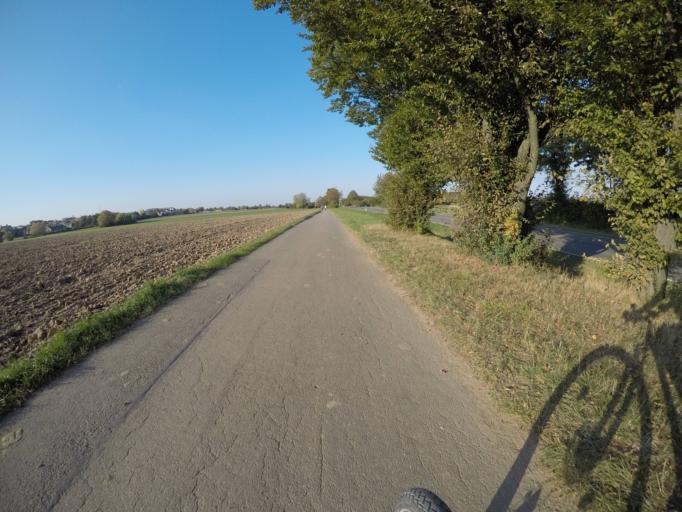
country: DE
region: Baden-Wuerttemberg
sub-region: Regierungsbezirk Stuttgart
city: Ostfildern
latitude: 48.7314
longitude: 9.2359
